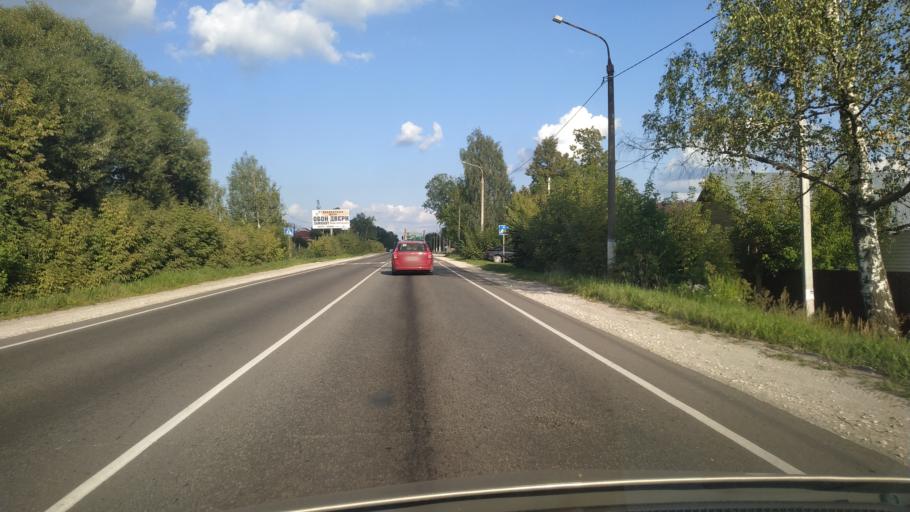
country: RU
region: Moskovskaya
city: Shaturtorf
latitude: 55.5795
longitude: 39.4726
